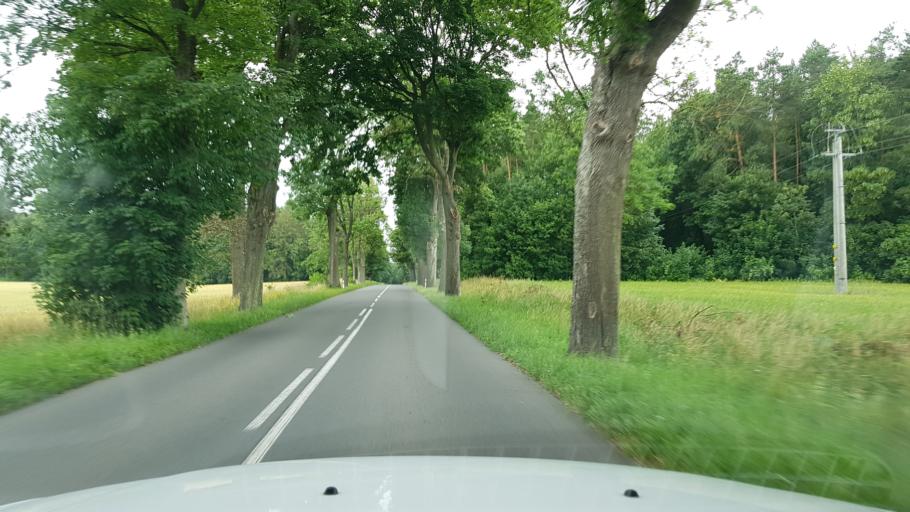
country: PL
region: West Pomeranian Voivodeship
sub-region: Powiat gryficki
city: Cerkwica
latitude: 53.9273
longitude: 15.0961
